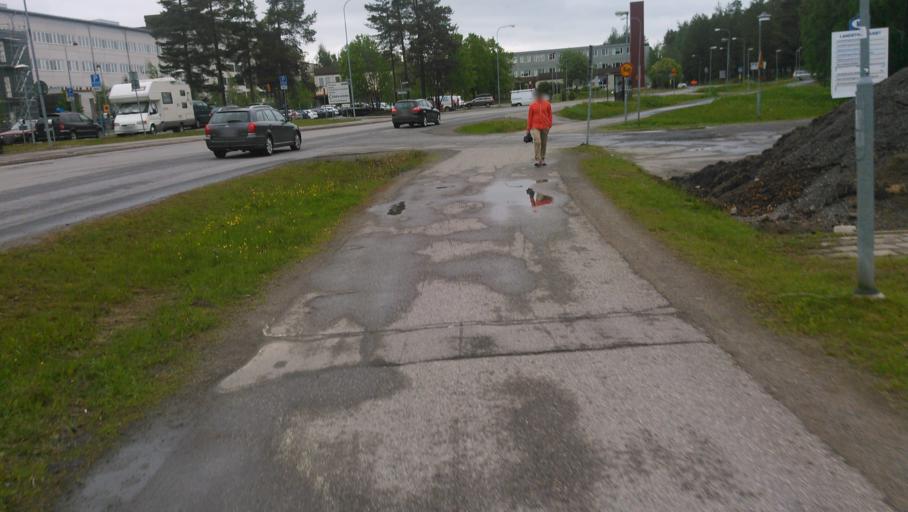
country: SE
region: Vaesterbotten
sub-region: Umea Kommun
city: Umea
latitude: 63.8147
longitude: 20.3032
